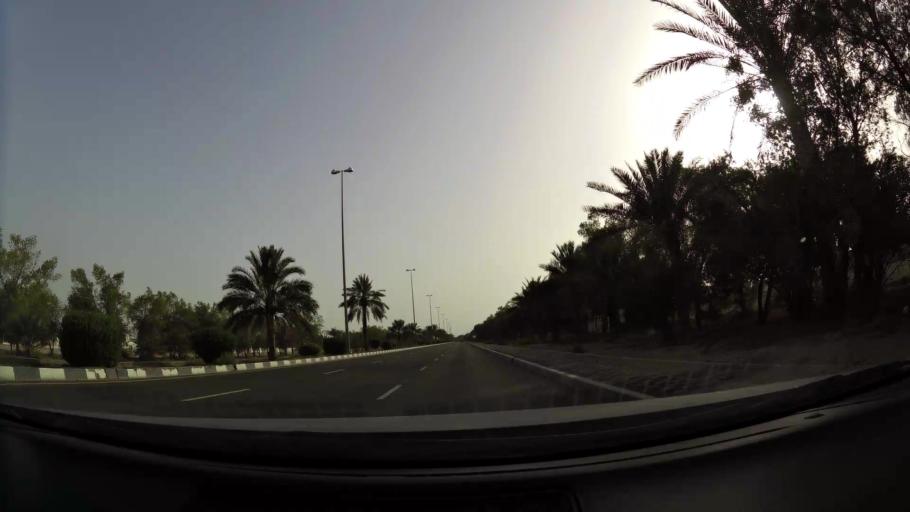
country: AE
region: Abu Dhabi
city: Al Ain
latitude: 24.1153
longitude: 55.7018
